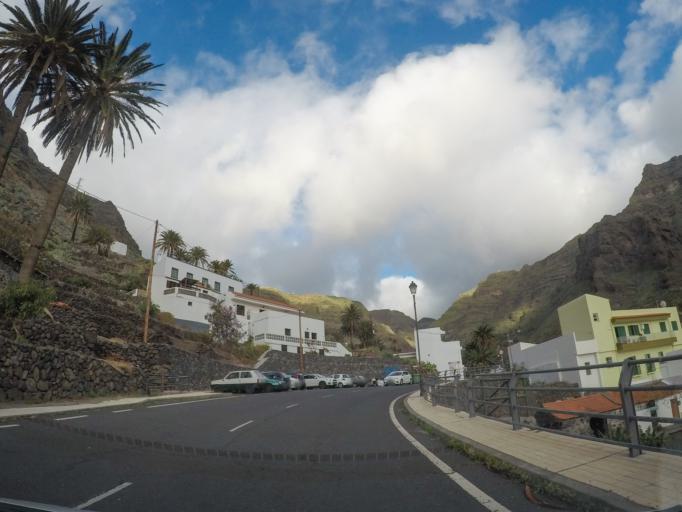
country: ES
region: Canary Islands
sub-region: Provincia de Santa Cruz de Tenerife
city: Vallehermosa
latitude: 28.1115
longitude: -17.3191
